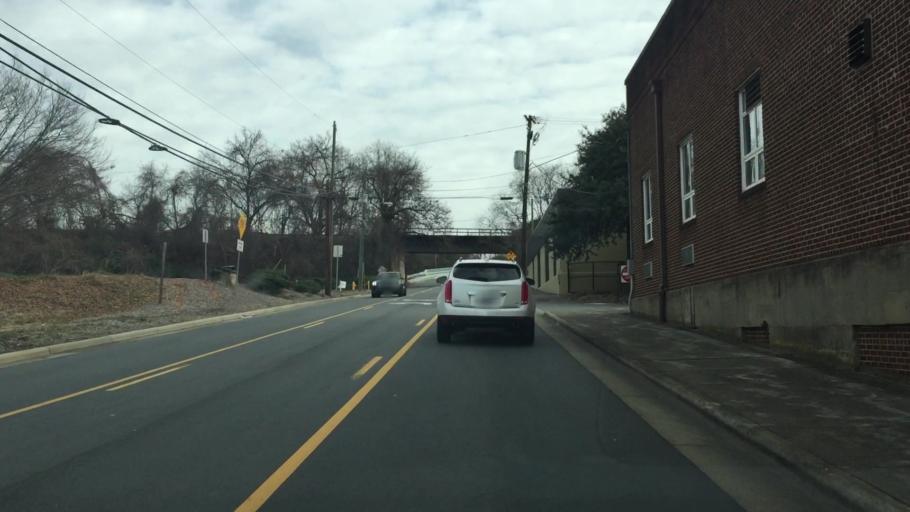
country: US
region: North Carolina
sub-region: Forsyth County
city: Winston-Salem
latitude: 36.0902
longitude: -80.2316
